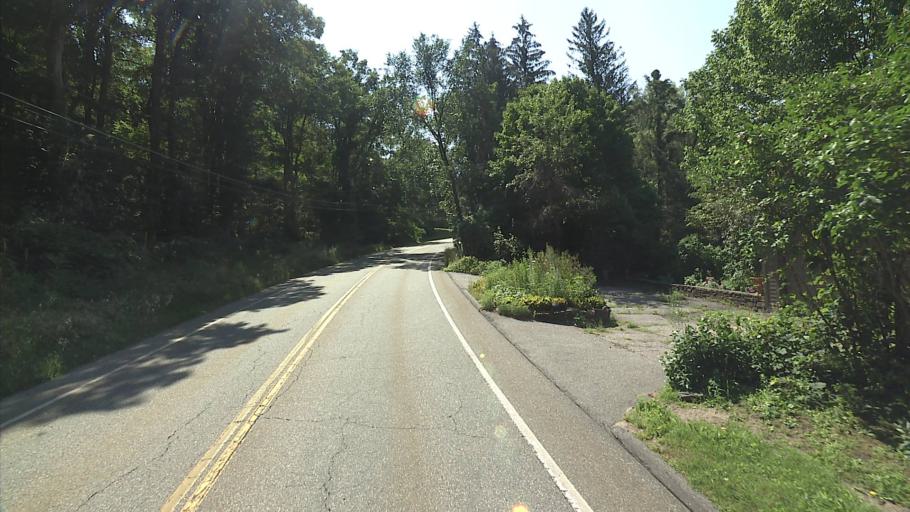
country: US
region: Connecticut
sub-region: Litchfield County
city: New Preston
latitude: 41.7980
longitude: -73.3709
